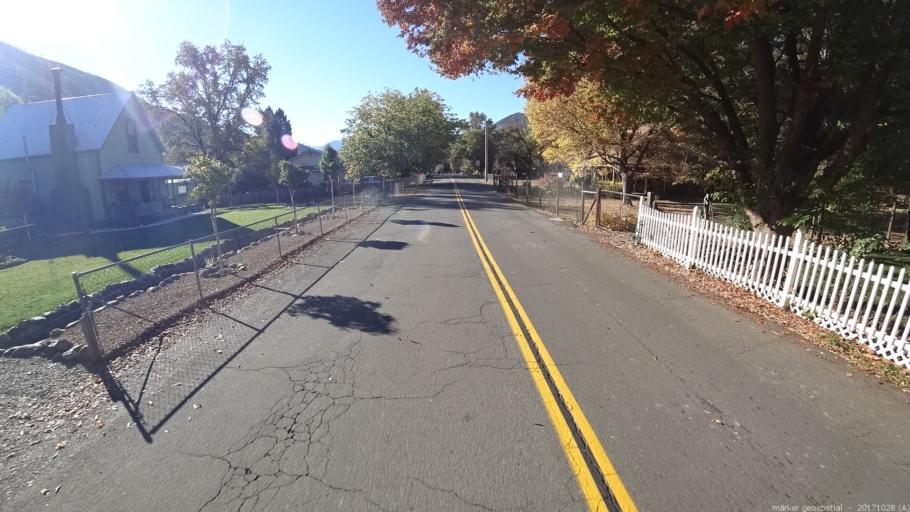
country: US
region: California
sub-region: Trinity County
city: Lewiston
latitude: 40.7028
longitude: -122.6377
